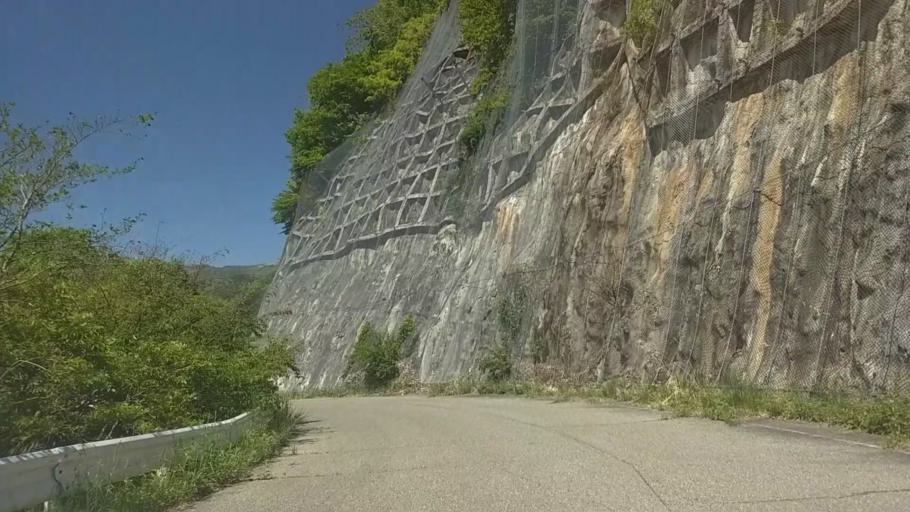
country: JP
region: Yamanashi
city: Nirasaki
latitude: 35.8787
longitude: 138.4532
